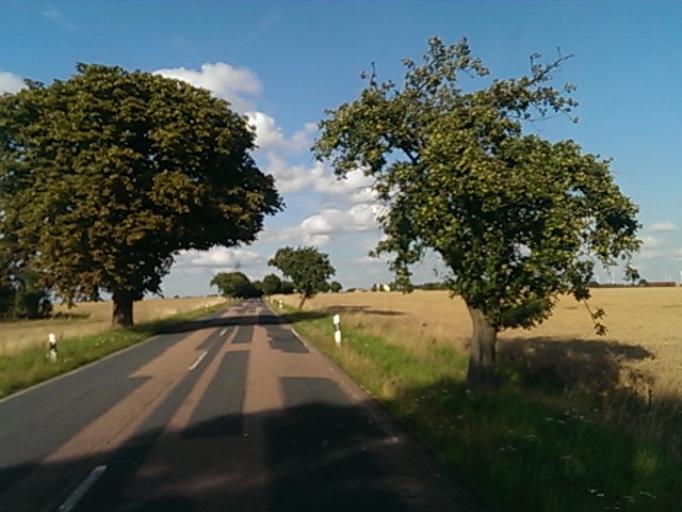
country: DE
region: Saxony-Anhalt
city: Nudersdorf
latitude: 51.9667
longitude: 12.5532
